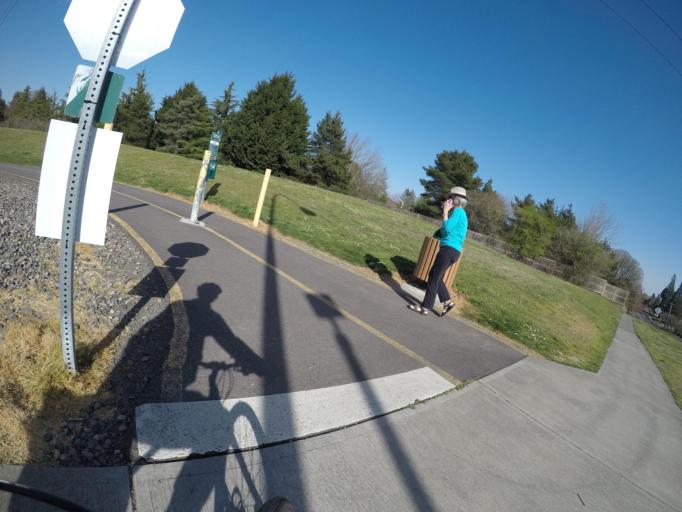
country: US
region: Oregon
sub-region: Washington County
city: Oak Hills
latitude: 45.5514
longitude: -122.8475
